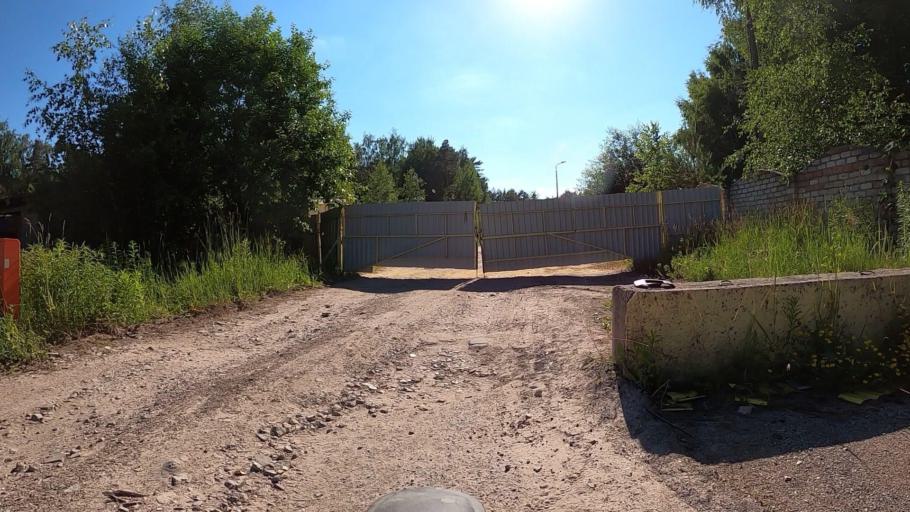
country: LV
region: Stopini
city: Ulbroka
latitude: 56.8789
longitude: 24.2752
